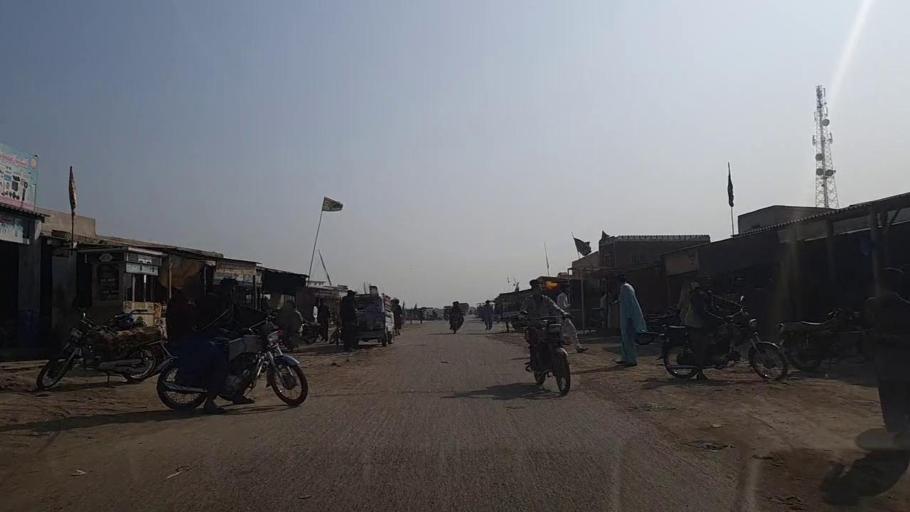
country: PK
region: Sindh
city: Keti Bandar
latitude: 24.2380
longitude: 67.6075
